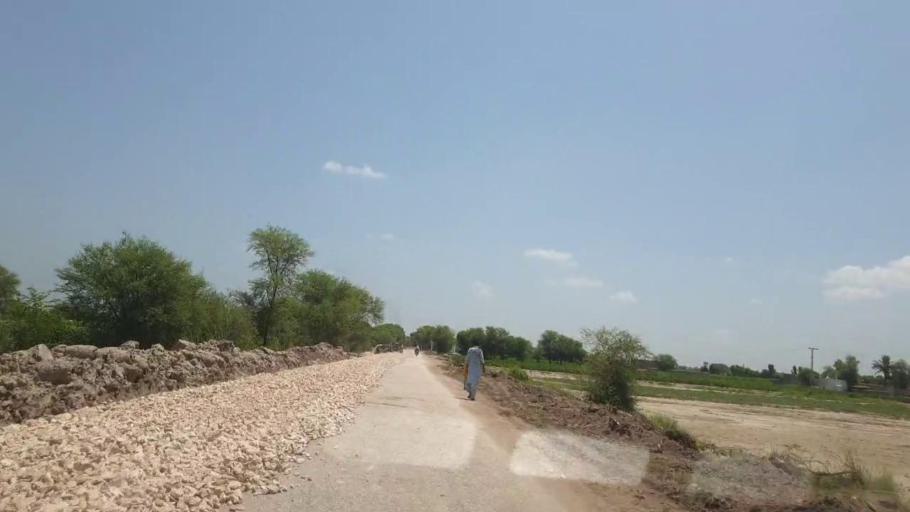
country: PK
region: Sindh
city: Pano Aqil
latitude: 27.6660
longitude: 69.1859
